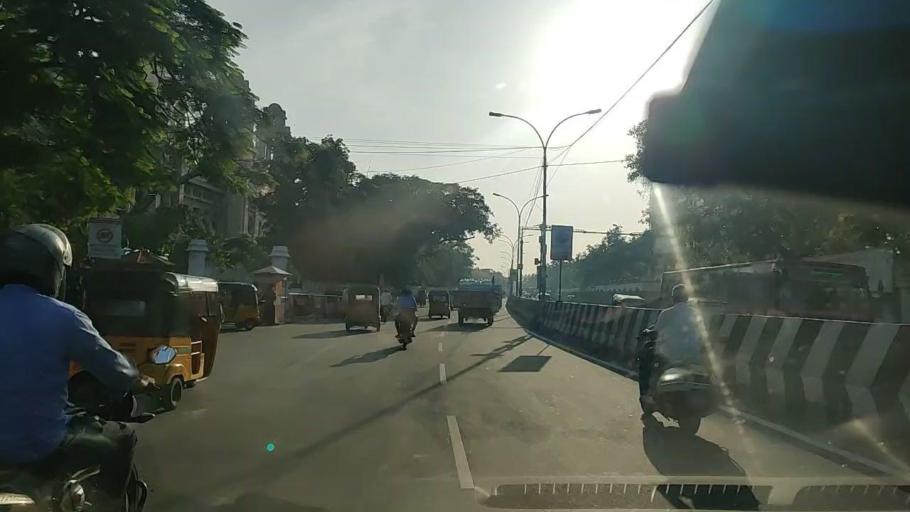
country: IN
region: Tamil Nadu
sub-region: Chennai
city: Chennai
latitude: 13.0817
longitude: 80.2760
